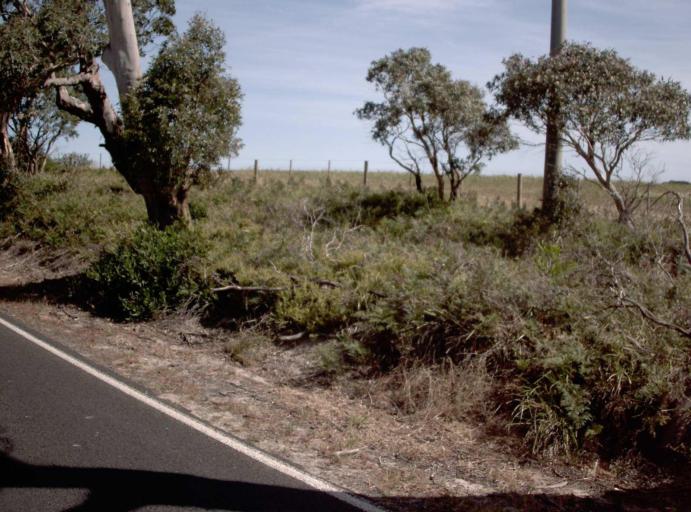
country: AU
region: Victoria
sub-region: Wellington
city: Sale
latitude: -38.3403
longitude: 147.1661
